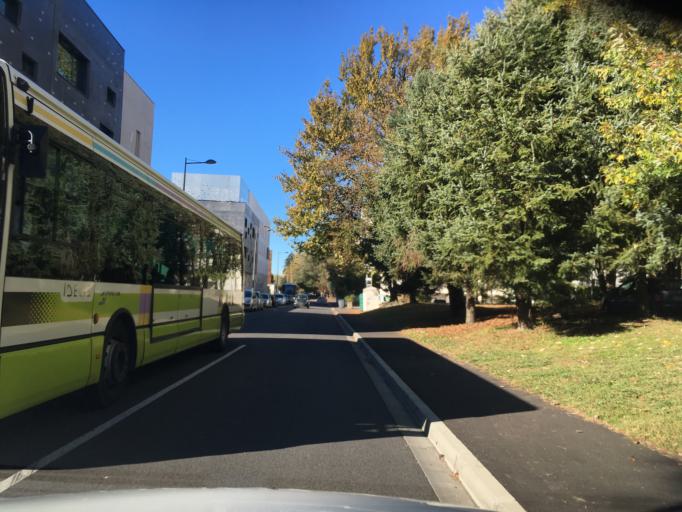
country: FR
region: Aquitaine
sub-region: Departement des Pyrenees-Atlantiques
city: Pau
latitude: 43.3054
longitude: -0.3613
